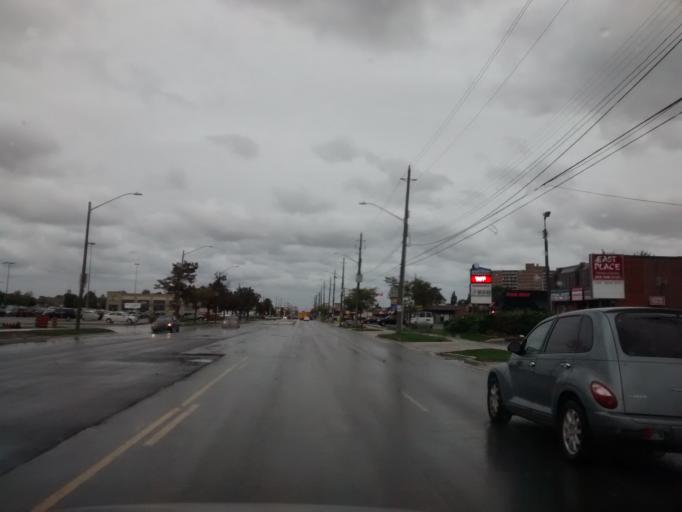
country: CA
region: Ontario
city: Hamilton
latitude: 43.2293
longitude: -79.7637
